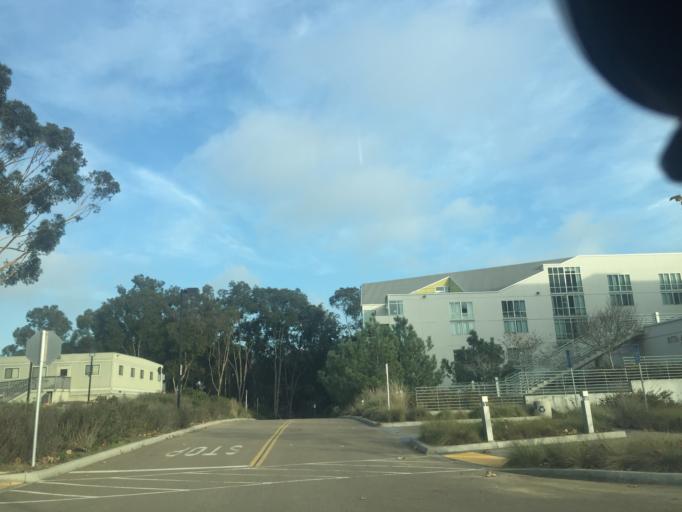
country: US
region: California
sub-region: San Diego County
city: La Jolla
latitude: 32.8731
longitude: -117.2357
